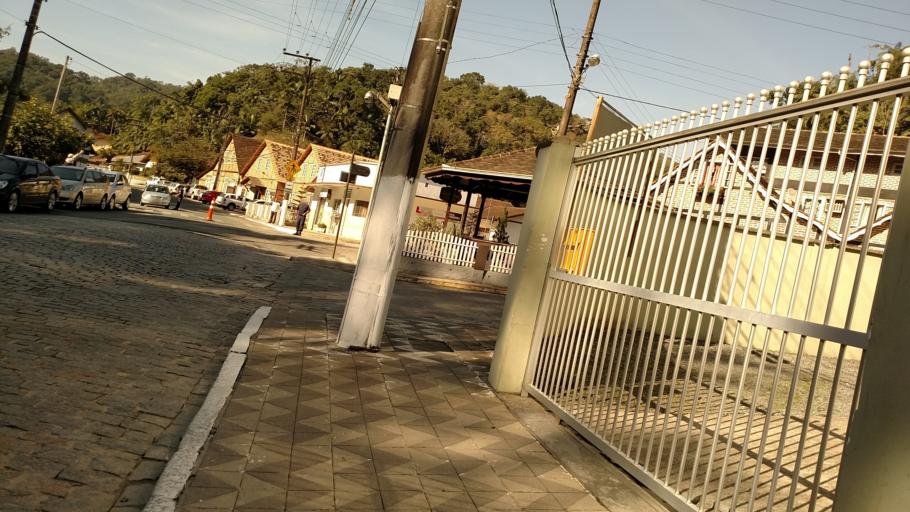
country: BR
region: Santa Catarina
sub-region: Pomerode
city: Pomerode
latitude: -26.7313
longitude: -49.0692
